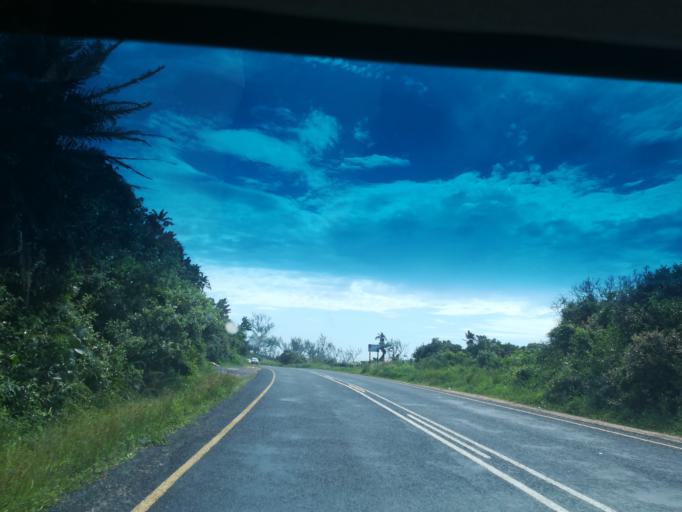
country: ZA
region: KwaZulu-Natal
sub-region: Ugu District Municipality
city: Scottburgh
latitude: -30.3404
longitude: 30.7312
